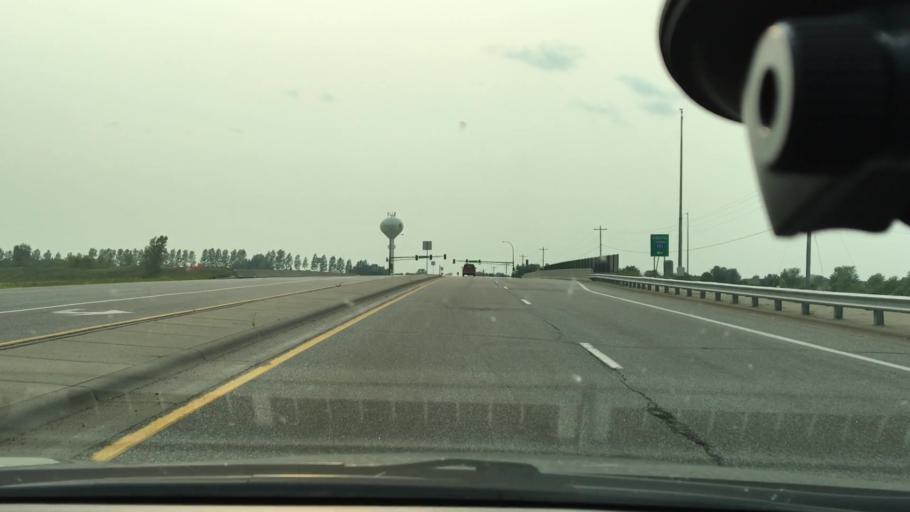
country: US
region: Minnesota
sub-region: Hennepin County
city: Dayton
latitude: 45.2525
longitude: -93.5538
